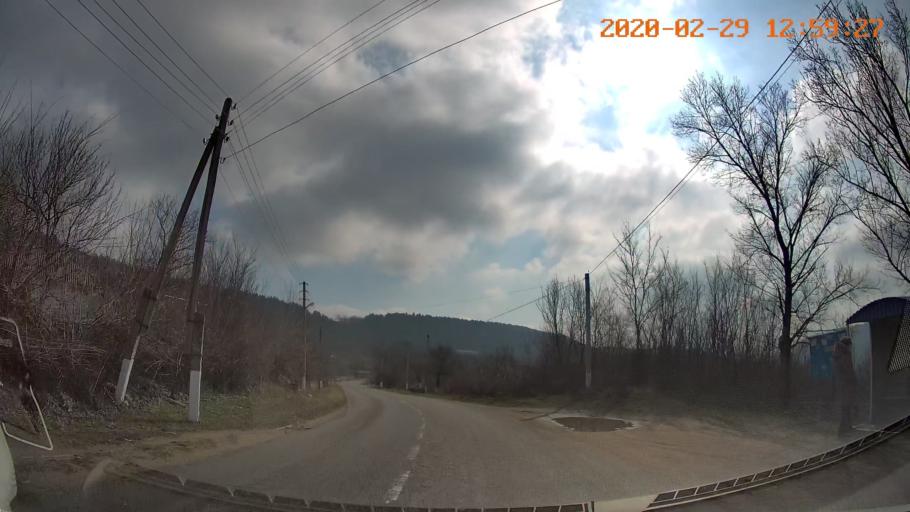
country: MD
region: Telenesti
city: Camenca
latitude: 48.0619
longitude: 28.7240
